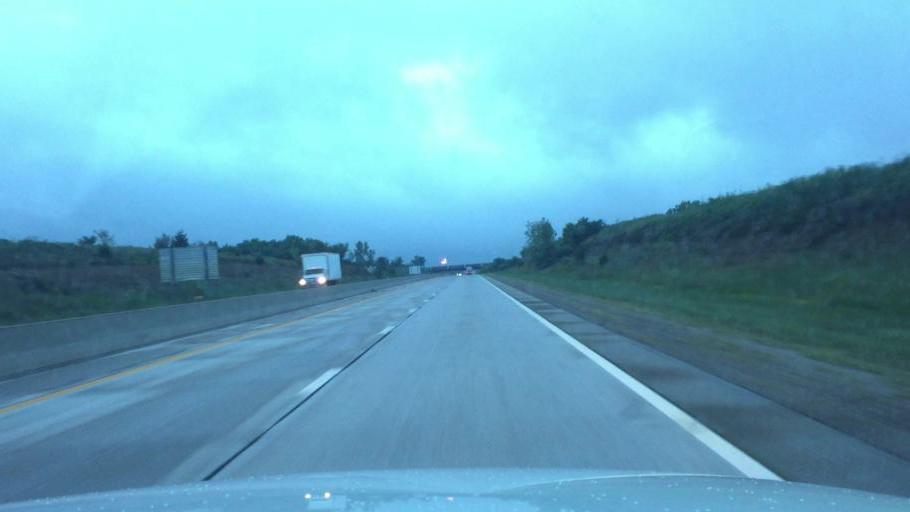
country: US
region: Kansas
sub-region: Neosho County
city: Chanute
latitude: 37.6702
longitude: -95.4795
